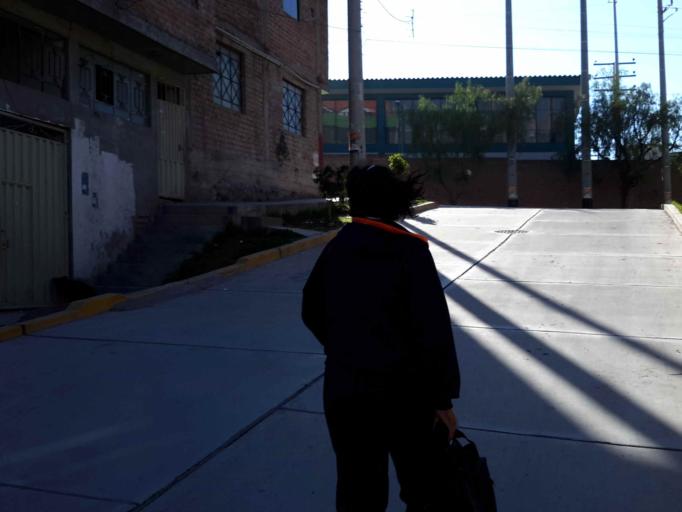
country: PE
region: Ayacucho
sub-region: Provincia de Huamanga
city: Ayacucho
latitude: -13.1528
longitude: -74.2215
